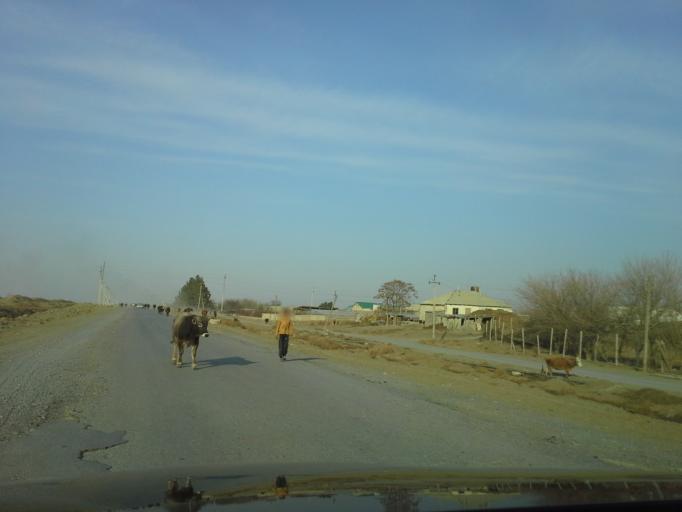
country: TM
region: Ahal
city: Abadan
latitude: 38.1771
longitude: 58.0386
